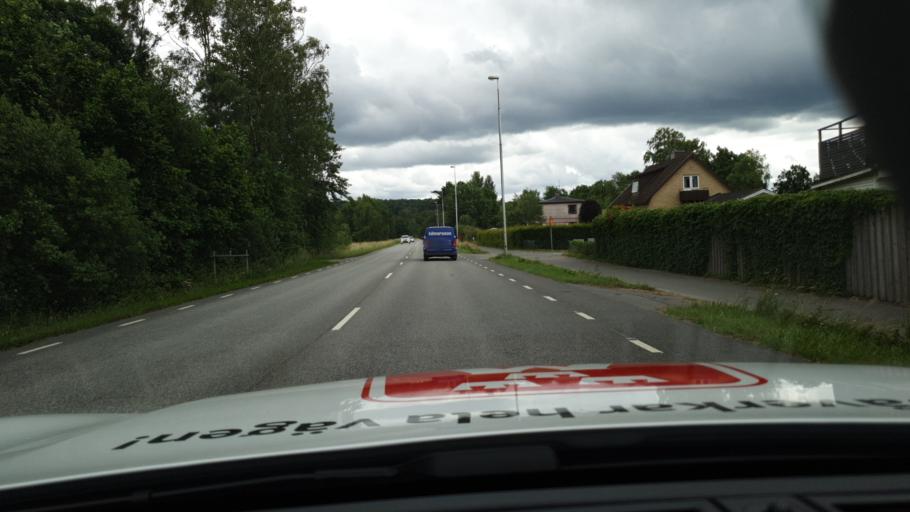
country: SE
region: Skane
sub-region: Hassleholms Kommun
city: Tormestorp
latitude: 56.1328
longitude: 13.7394
